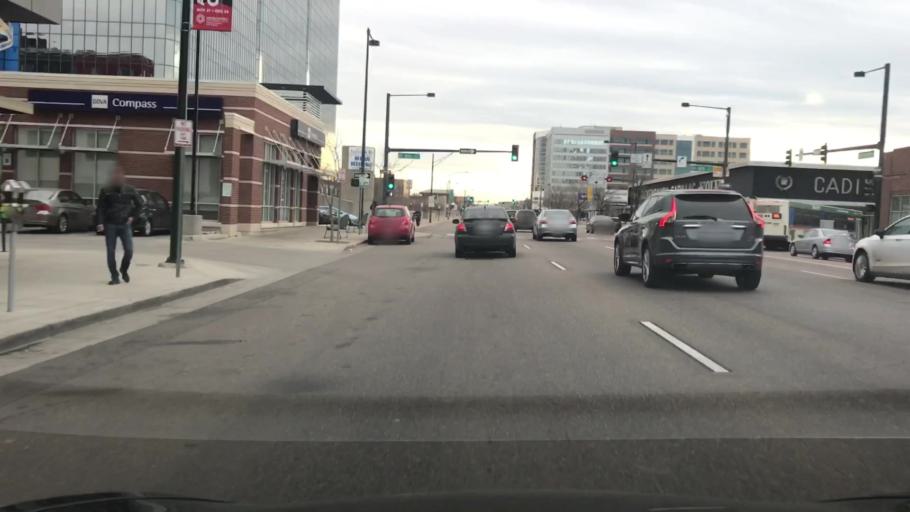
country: US
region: Colorado
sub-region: Denver County
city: Denver
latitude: 39.7296
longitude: -104.9873
